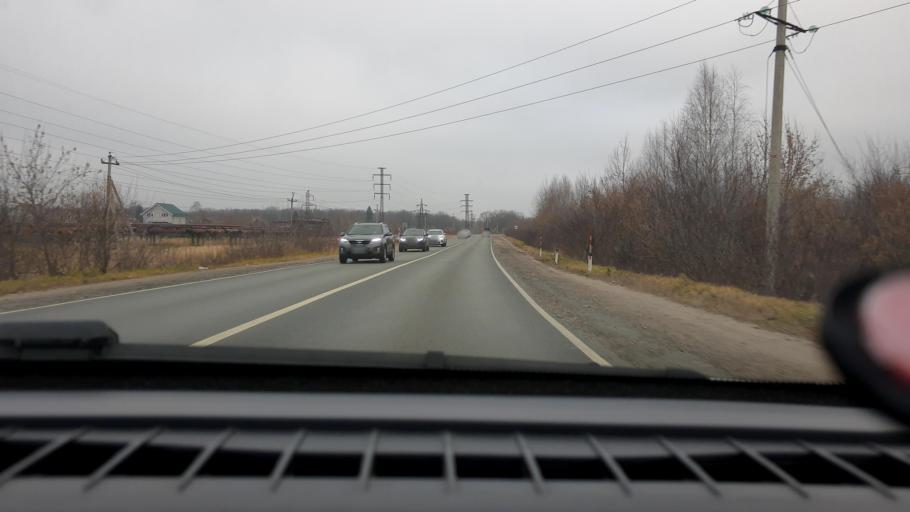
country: RU
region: Nizjnij Novgorod
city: Novaya Balakhna
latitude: 56.5083
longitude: 43.5837
